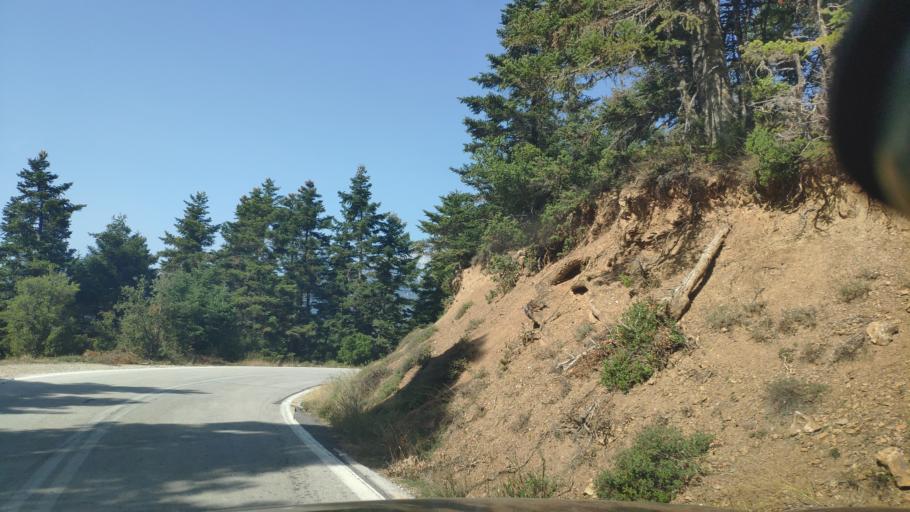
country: GR
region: West Greece
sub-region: Nomos Achaias
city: Aiyira
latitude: 37.8699
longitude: 22.3605
